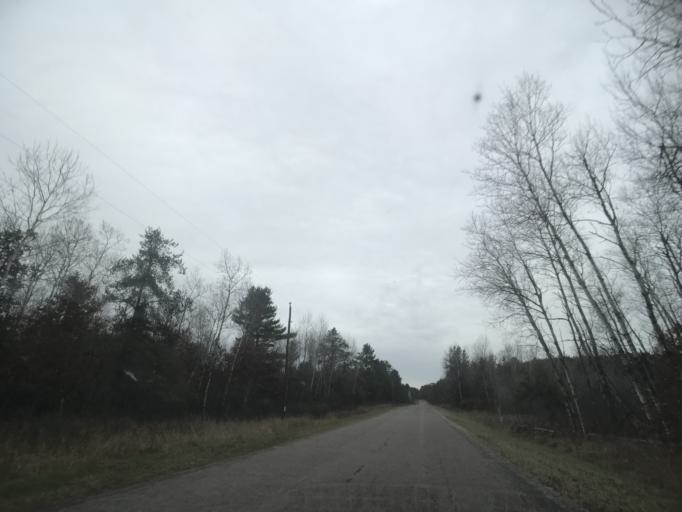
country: US
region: Wisconsin
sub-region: Oconto County
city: Gillett
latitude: 45.2767
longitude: -88.2571
